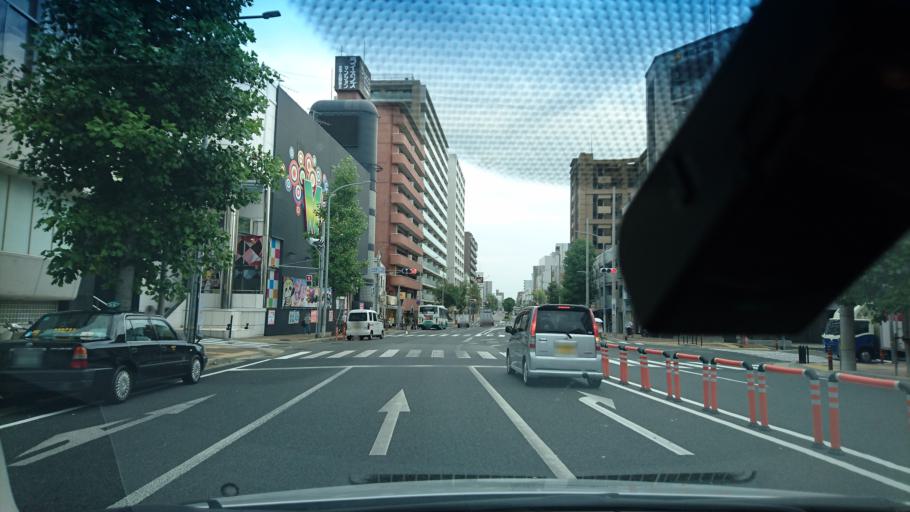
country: JP
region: Hyogo
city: Kobe
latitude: 34.7128
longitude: 135.2244
